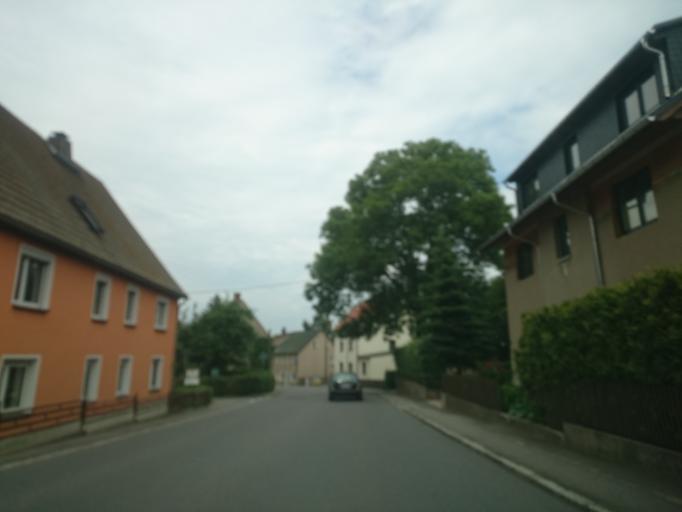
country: DE
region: Saxony
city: Eppendorf
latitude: 50.7931
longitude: 13.2287
